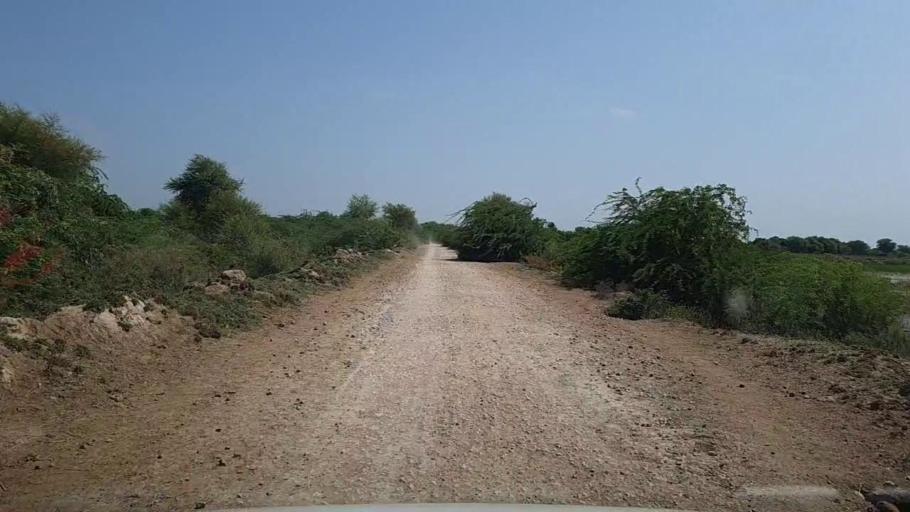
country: PK
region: Sindh
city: Kario
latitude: 24.8382
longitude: 68.7074
